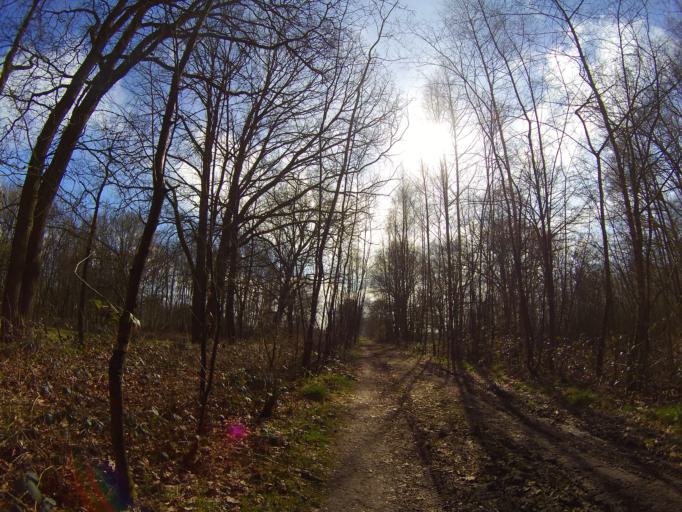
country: NL
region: Utrecht
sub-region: Gemeente Woudenberg
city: Woudenberg
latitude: 52.0991
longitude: 5.4333
